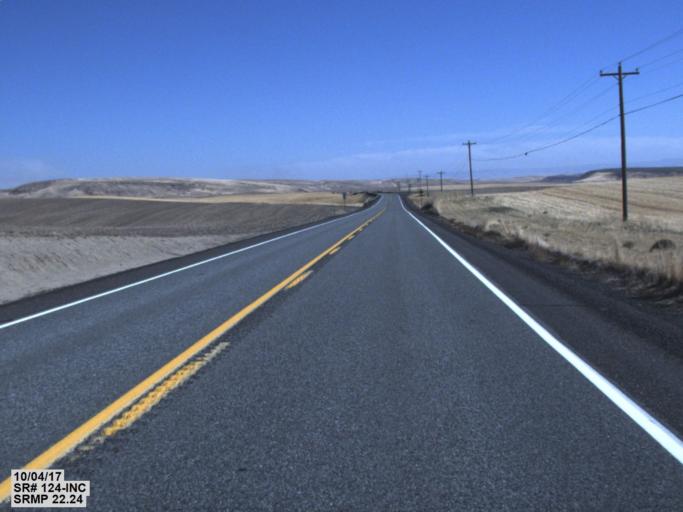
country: US
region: Washington
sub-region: Walla Walla County
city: Garrett
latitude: 46.2962
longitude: -118.5914
